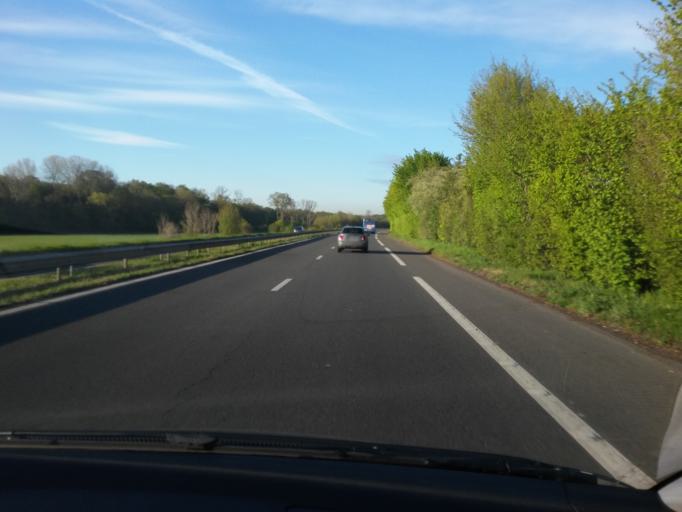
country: FR
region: Picardie
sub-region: Departement de l'Oise
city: Jaux
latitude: 49.3750
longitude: 2.7806
